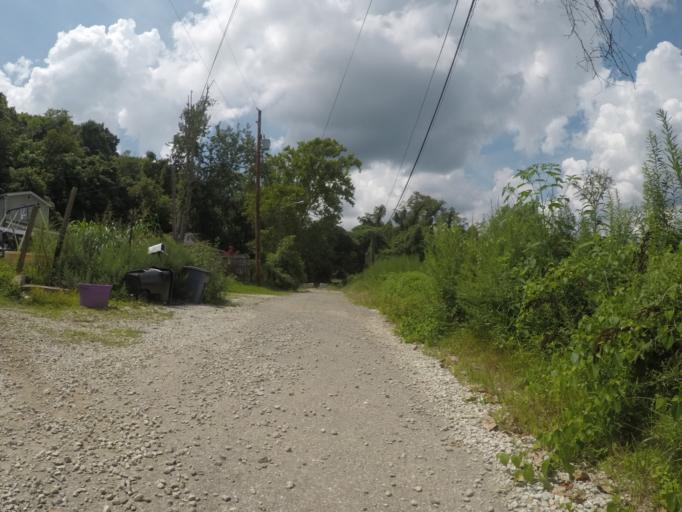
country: US
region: West Virginia
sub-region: Cabell County
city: Pea Ridge
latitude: 38.4259
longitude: -82.3791
